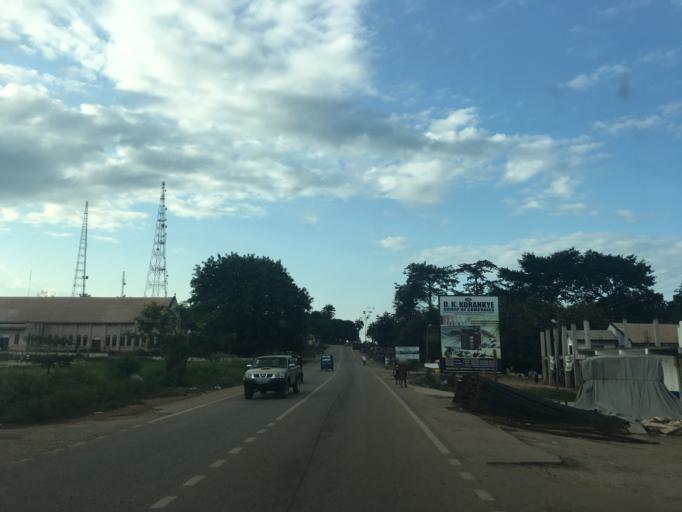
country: GH
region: Western
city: Bibiani
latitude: 6.4562
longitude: -2.3174
